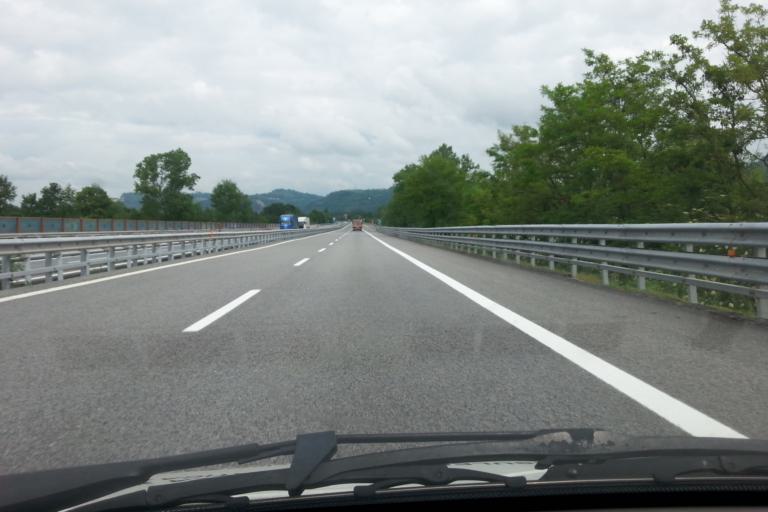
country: IT
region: Piedmont
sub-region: Provincia di Cuneo
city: Lesegno
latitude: 44.4031
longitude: 7.9729
